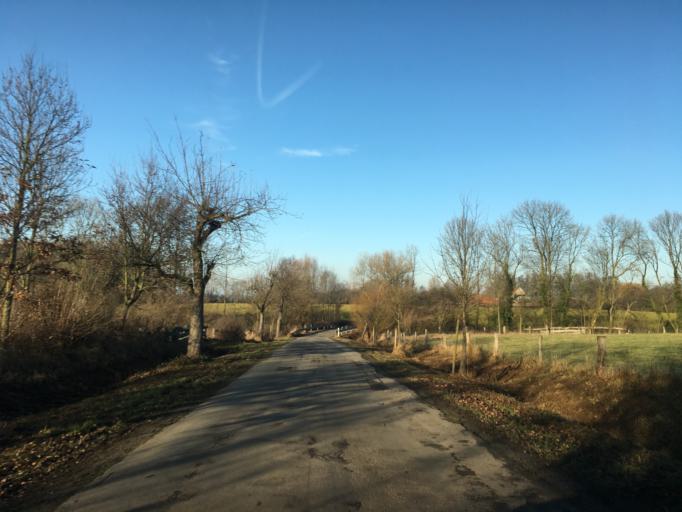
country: DE
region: North Rhine-Westphalia
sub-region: Regierungsbezirk Munster
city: Altenberge
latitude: 52.0370
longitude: 7.5227
